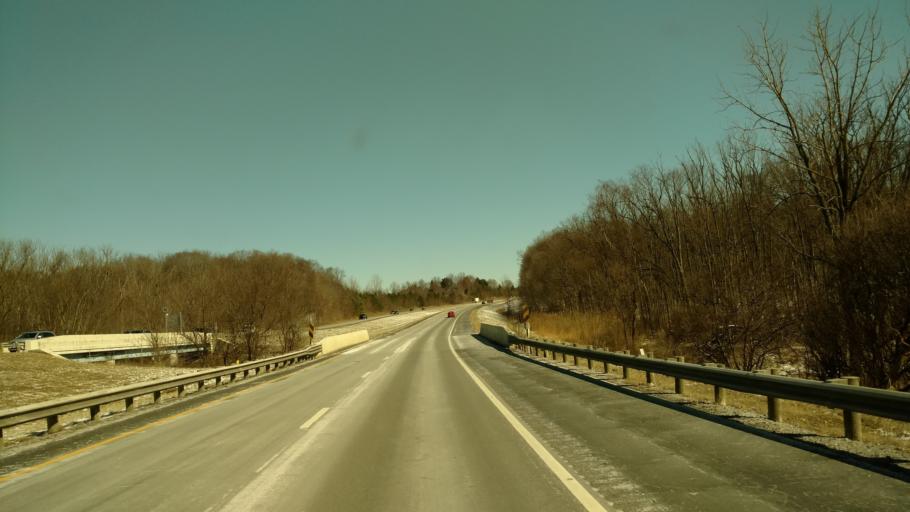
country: US
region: Ohio
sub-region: Medina County
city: Brunswick
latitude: 41.1804
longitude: -81.7585
